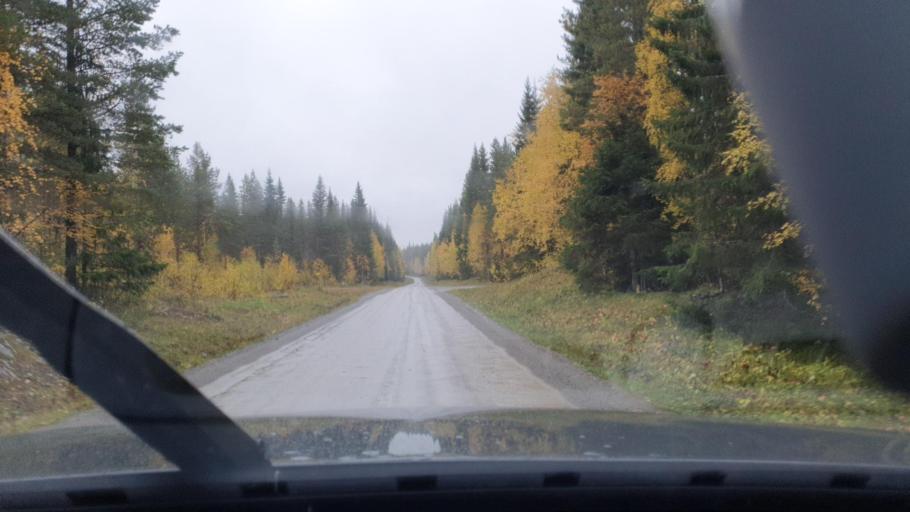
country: SE
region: Jaemtland
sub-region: Stroemsunds Kommun
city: Stroemsund
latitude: 63.5350
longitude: 15.6090
